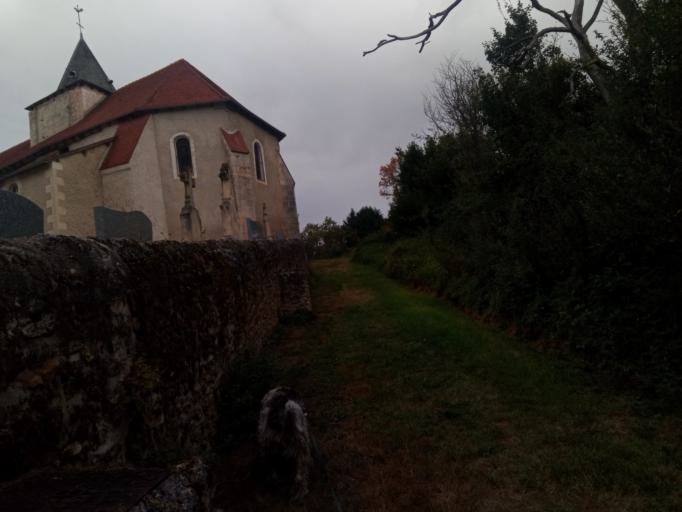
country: FR
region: Poitou-Charentes
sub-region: Departement de la Vienne
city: Montmorillon
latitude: 46.4904
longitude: 0.8128
